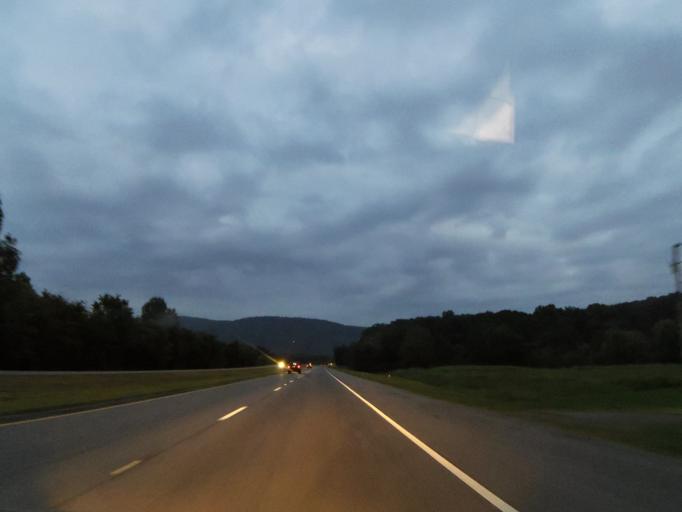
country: US
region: Alabama
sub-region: Madison County
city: Owens Cross Roads
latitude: 34.6831
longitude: -86.3360
